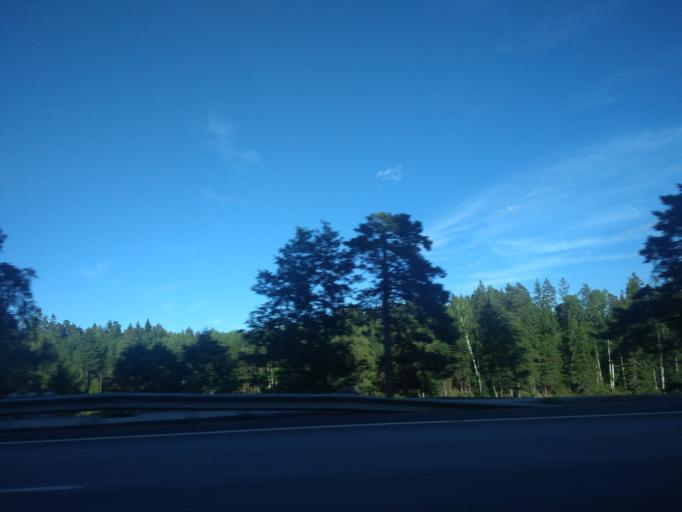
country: SE
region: OEstergoetland
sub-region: Norrkopings Kommun
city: Jursla
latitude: 58.7502
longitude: 16.1764
